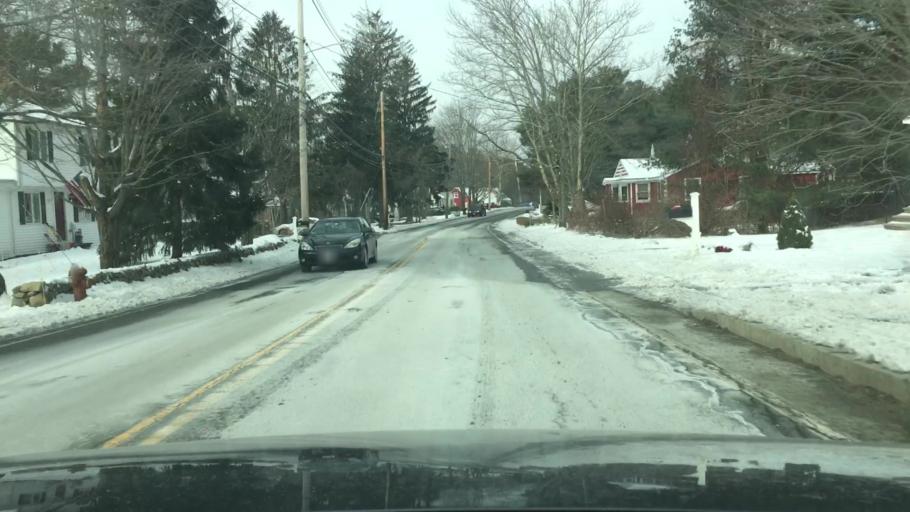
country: US
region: Massachusetts
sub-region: Middlesex County
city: North Reading
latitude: 42.5726
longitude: -71.0499
